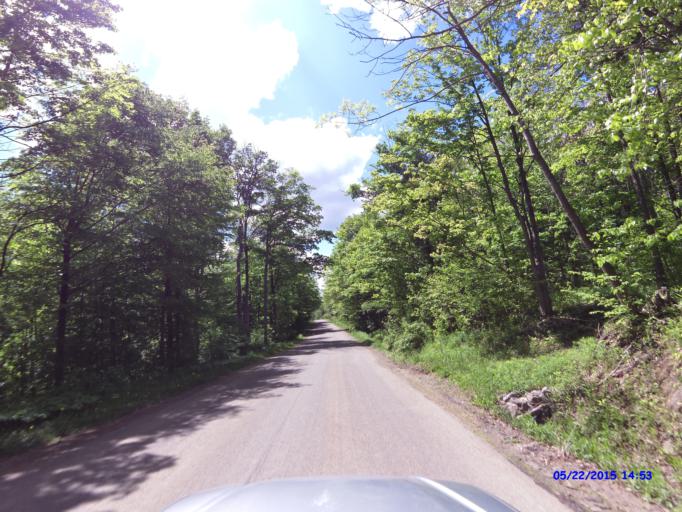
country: US
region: New York
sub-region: Cattaraugus County
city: Franklinville
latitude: 42.3808
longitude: -78.5861
